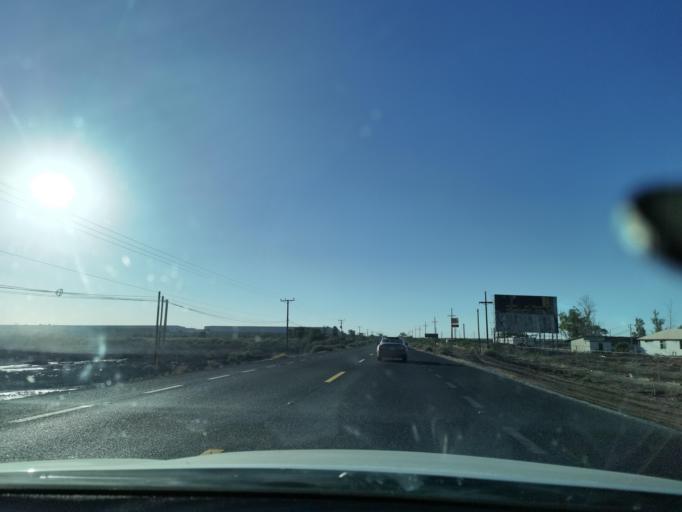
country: MX
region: Baja California
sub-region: Mexicali
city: Islas Agrarias Grupo A
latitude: 32.6373
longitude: -115.2875
